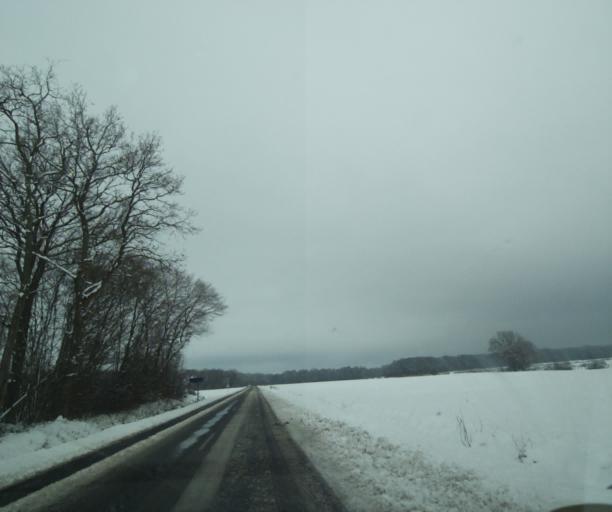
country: FR
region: Champagne-Ardenne
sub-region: Departement de la Haute-Marne
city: Montier-en-Der
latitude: 48.5091
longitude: 4.7479
